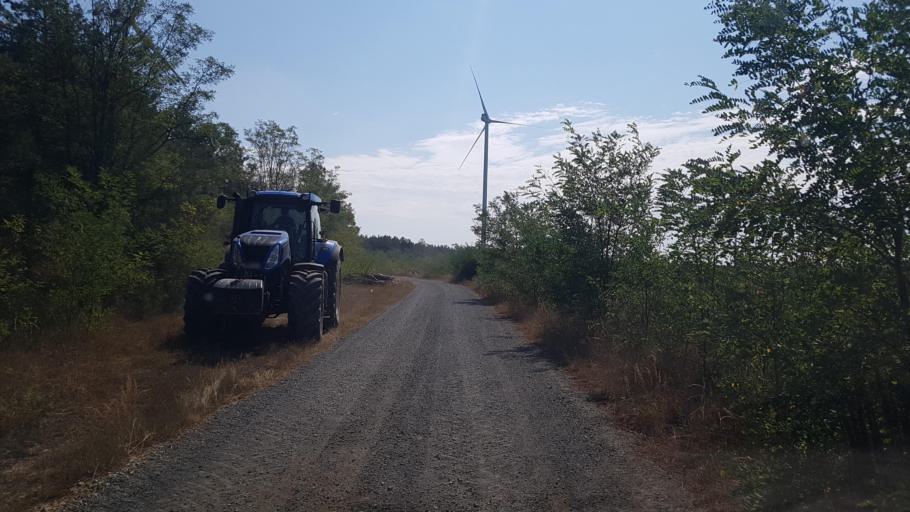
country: DE
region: Brandenburg
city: Schipkau
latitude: 51.5433
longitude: 13.8585
